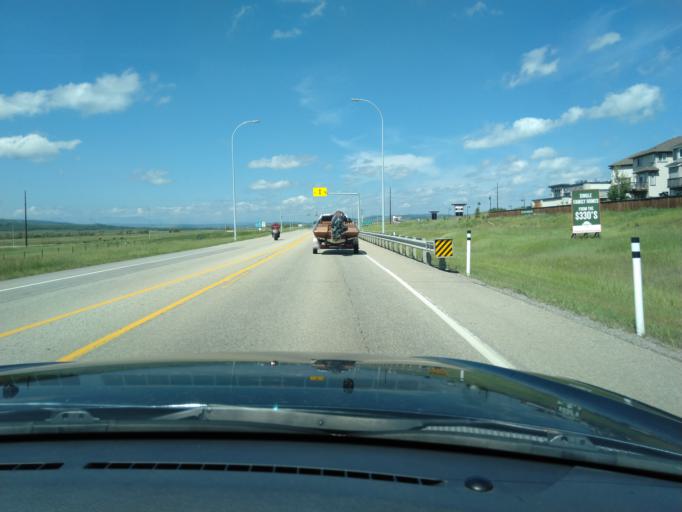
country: CA
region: Alberta
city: Cochrane
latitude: 51.2051
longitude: -114.5090
